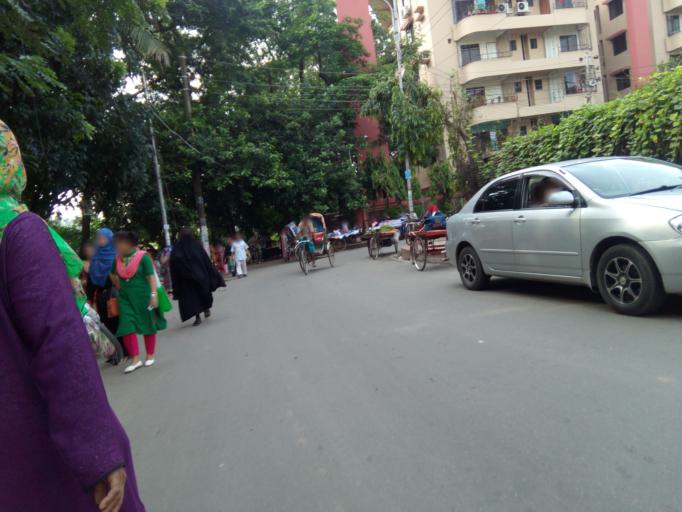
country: BD
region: Dhaka
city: Azimpur
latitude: 23.7446
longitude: 90.3770
